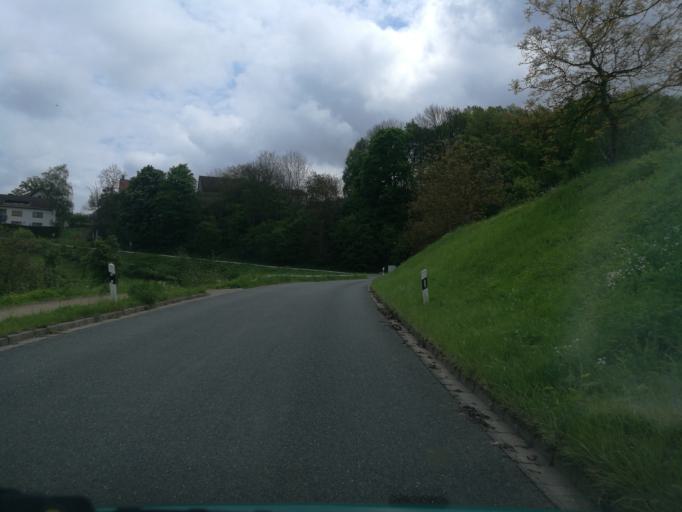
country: DE
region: Bavaria
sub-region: Upper Franconia
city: Bad Staffelstein
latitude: 50.1009
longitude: 11.0293
